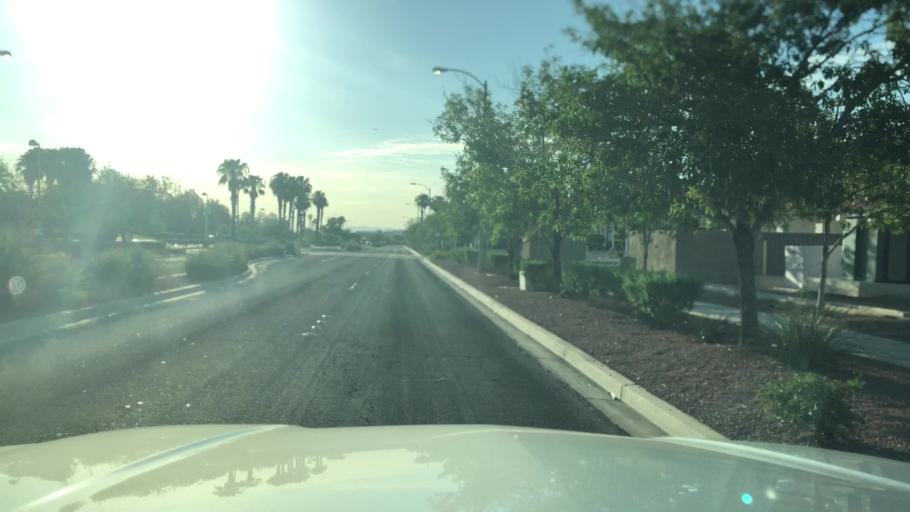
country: US
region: Nevada
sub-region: Clark County
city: Whitney
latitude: 36.0727
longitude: -115.0800
